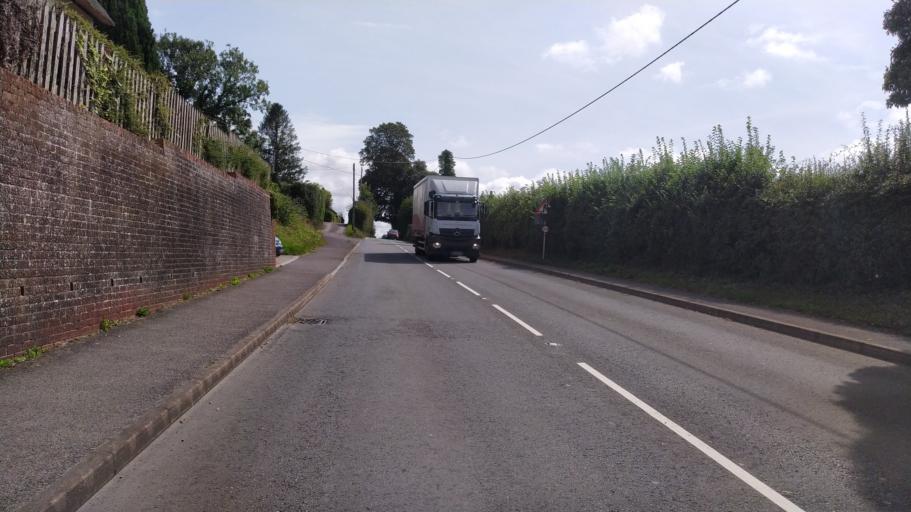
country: GB
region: England
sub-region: Dorset
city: Blandford Forum
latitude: 50.8836
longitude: -2.1977
